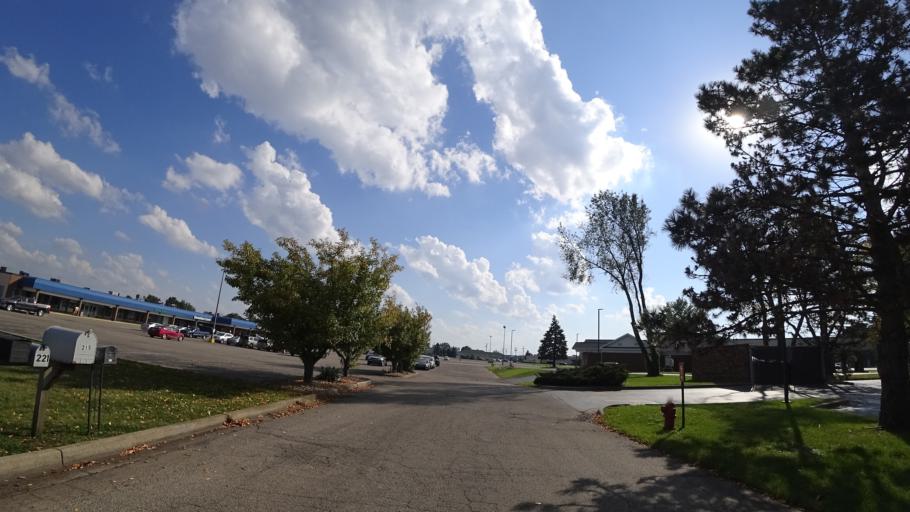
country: US
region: Michigan
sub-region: Saint Joseph County
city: Three Rivers
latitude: 41.9452
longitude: -85.6502
